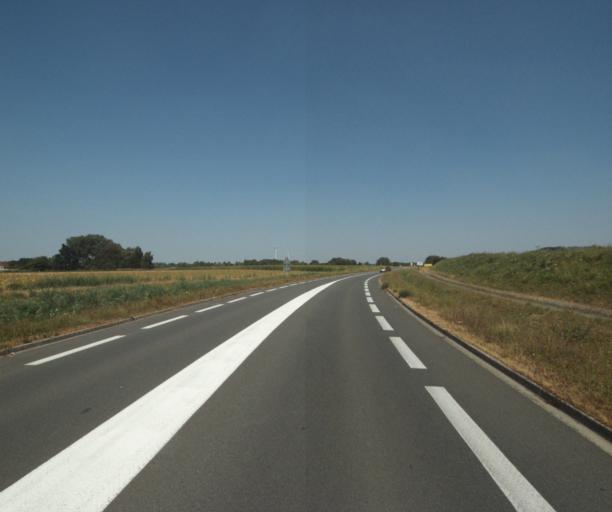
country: FR
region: Nord-Pas-de-Calais
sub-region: Departement du Nord
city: Bousbecque
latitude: 50.7705
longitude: 3.0928
